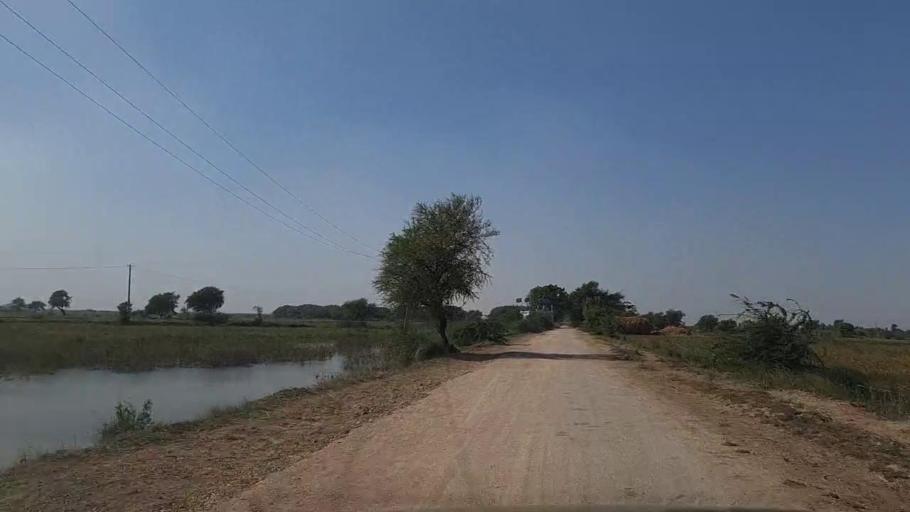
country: PK
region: Sindh
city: Daro Mehar
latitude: 24.8367
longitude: 68.1498
